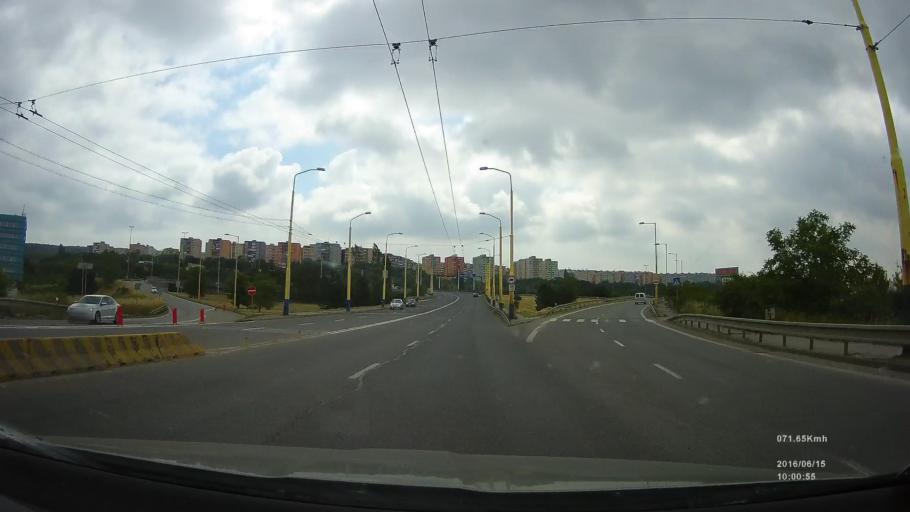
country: SK
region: Kosicky
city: Kosice
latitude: 48.7422
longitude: 21.2670
